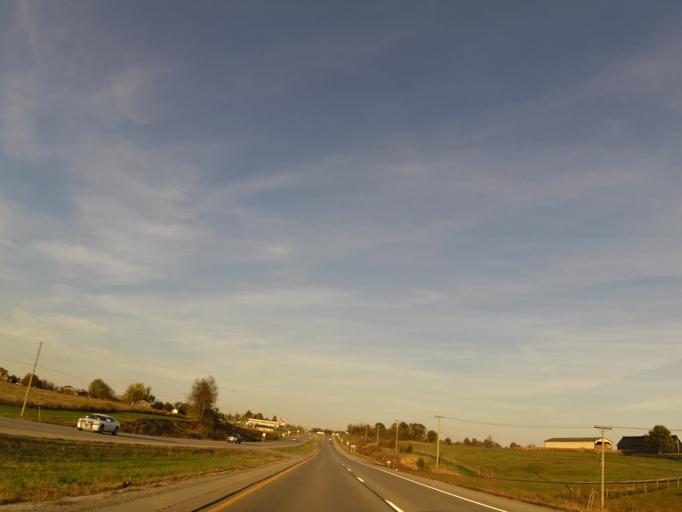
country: US
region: Kentucky
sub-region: Garrard County
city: Lancaster
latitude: 37.7039
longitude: -84.6601
